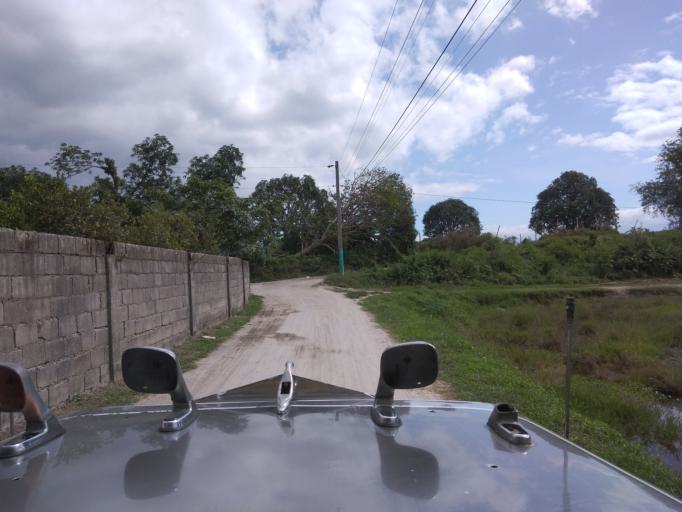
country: PH
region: Central Luzon
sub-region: Province of Pampanga
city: San Patricio
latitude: 15.1076
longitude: 120.7199
